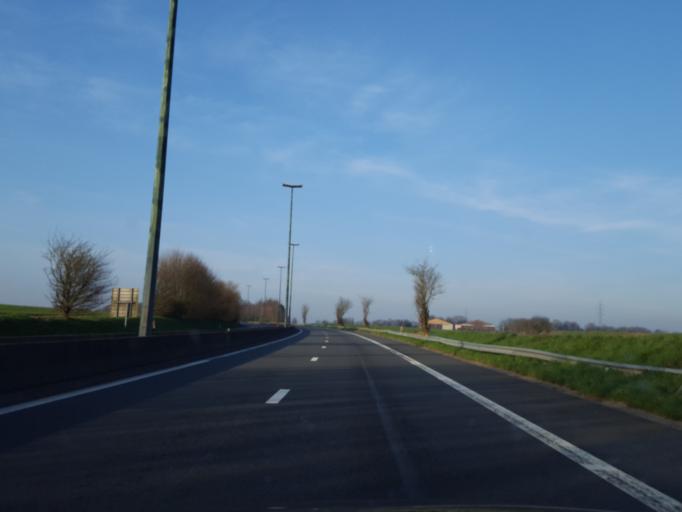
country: BE
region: Wallonia
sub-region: Province du Brabant Wallon
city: Genappe
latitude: 50.6112
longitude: 4.3963
